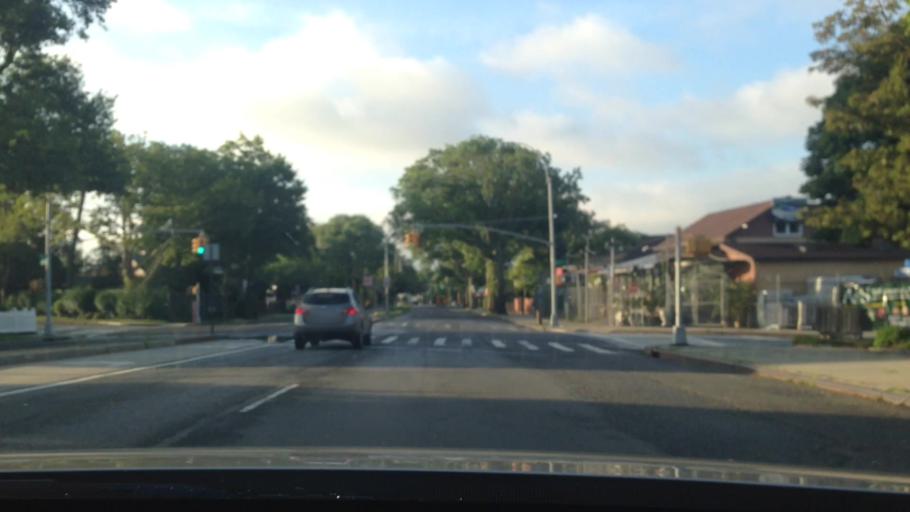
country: US
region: New York
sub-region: Nassau County
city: East Atlantic Beach
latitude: 40.7771
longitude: -73.8004
